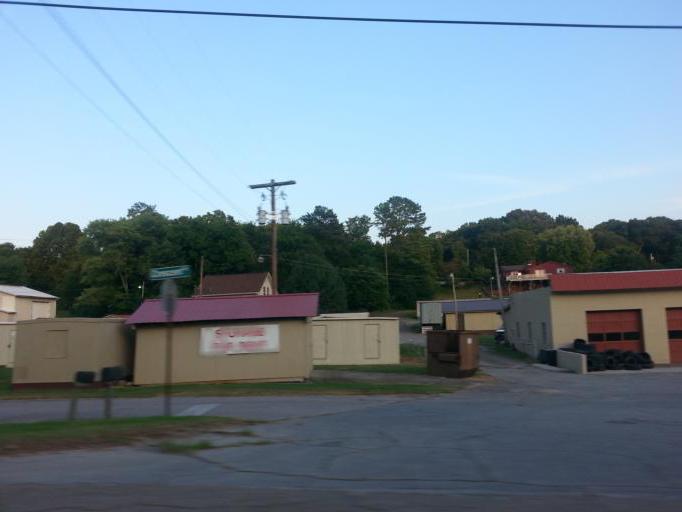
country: US
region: Tennessee
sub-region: Loudon County
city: Loudon
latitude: 35.7464
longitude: -84.3213
